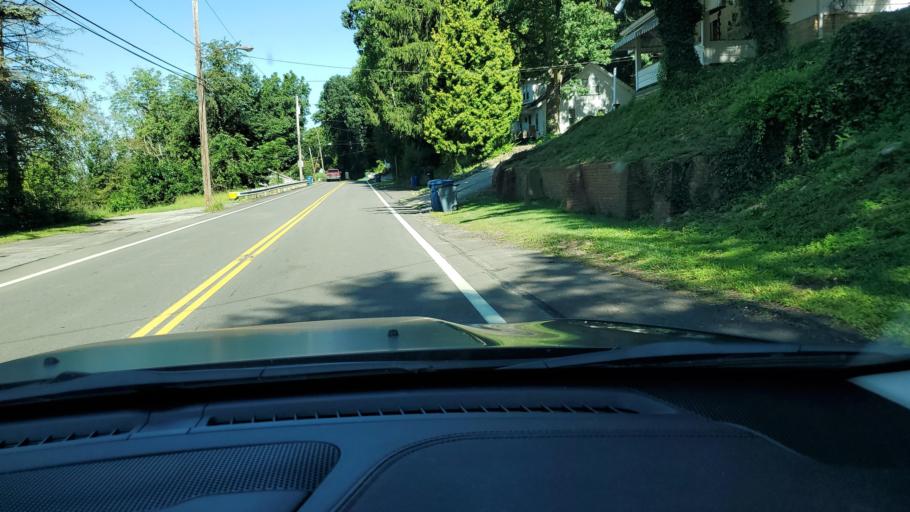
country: US
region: Ohio
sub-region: Mahoning County
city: Lowellville
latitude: 41.0445
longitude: -80.5474
